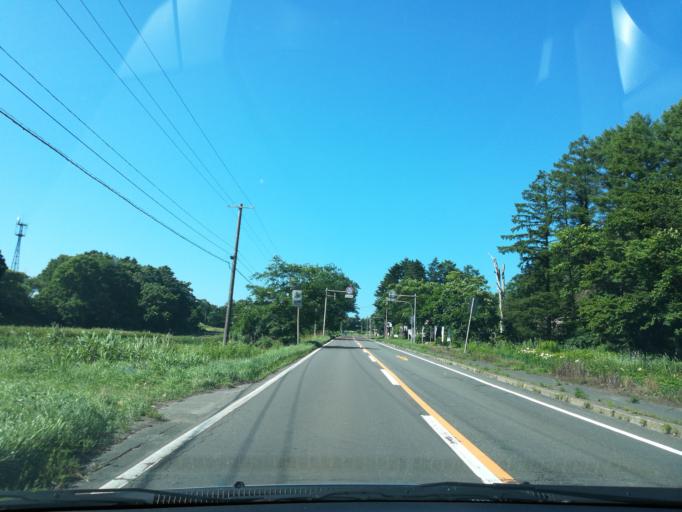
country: JP
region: Hokkaido
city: Chitose
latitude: 42.9117
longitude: 141.7268
